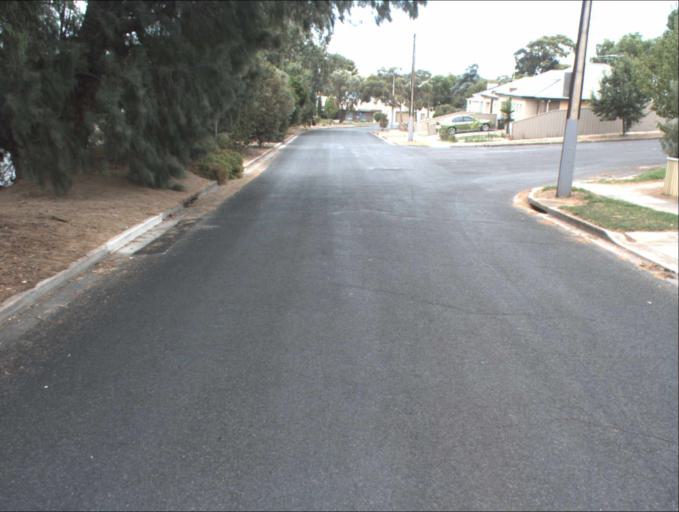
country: AU
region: South Australia
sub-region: Port Adelaide Enfield
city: Enfield
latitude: -34.8564
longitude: 138.6010
